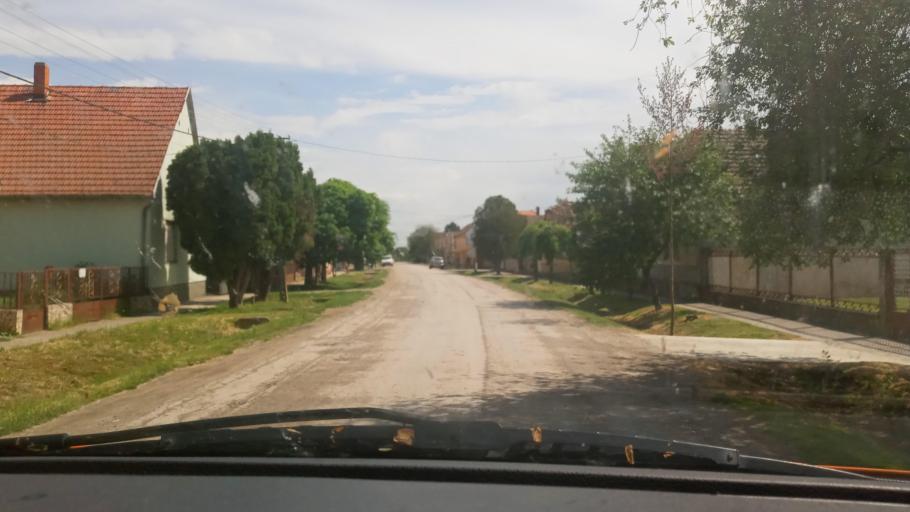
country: HU
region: Baranya
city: Beremend
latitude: 45.7902
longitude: 18.3511
